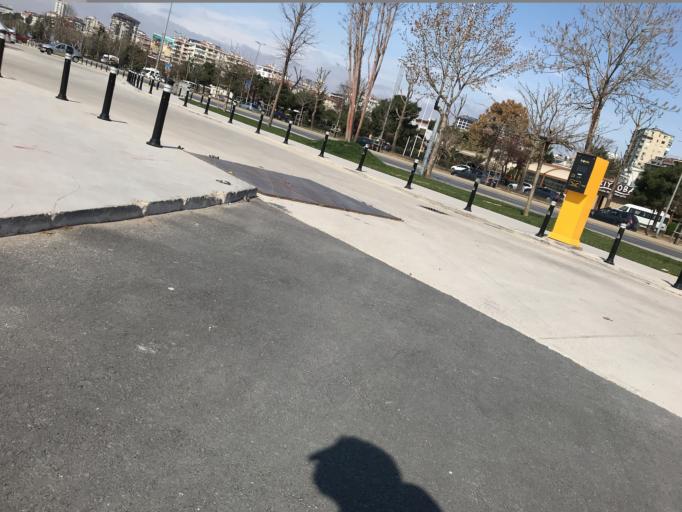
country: TR
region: Istanbul
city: Maltepe
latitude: 40.9236
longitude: 29.1248
